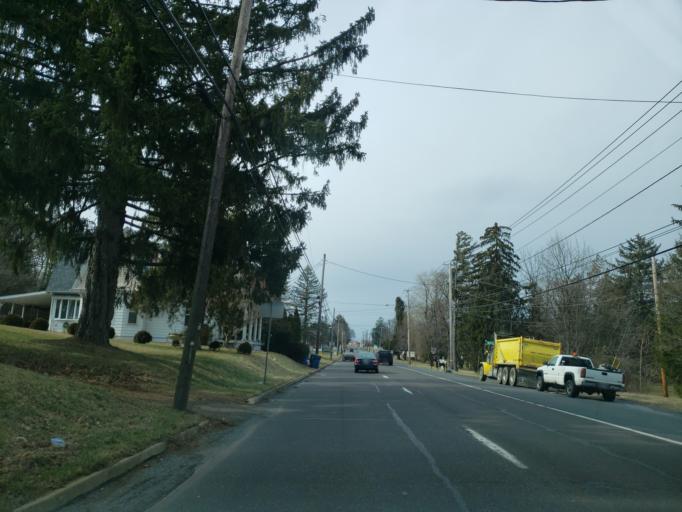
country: US
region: Pennsylvania
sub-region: Lehigh County
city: Coopersburg
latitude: 40.5306
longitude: -75.3976
